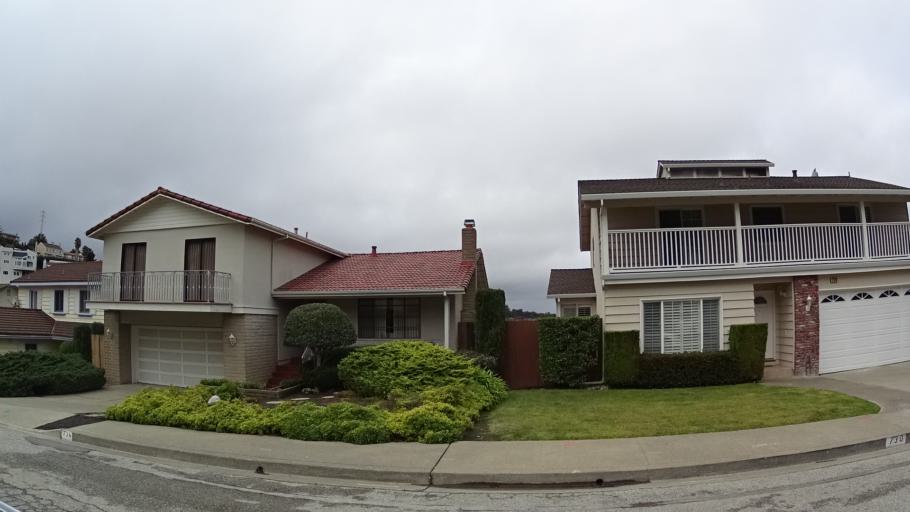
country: US
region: California
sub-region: San Mateo County
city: Millbrae
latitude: 37.5960
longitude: -122.4073
